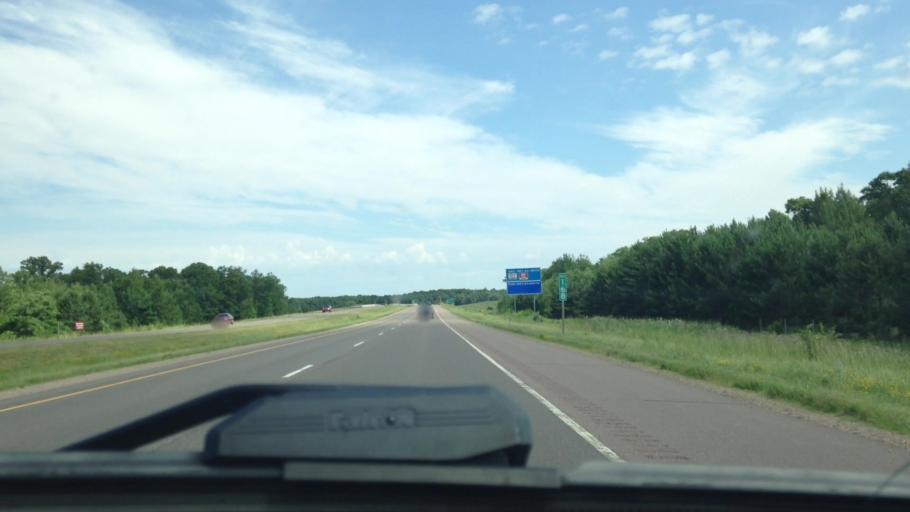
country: US
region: Wisconsin
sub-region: Washburn County
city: Spooner
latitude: 45.8469
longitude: -91.8604
